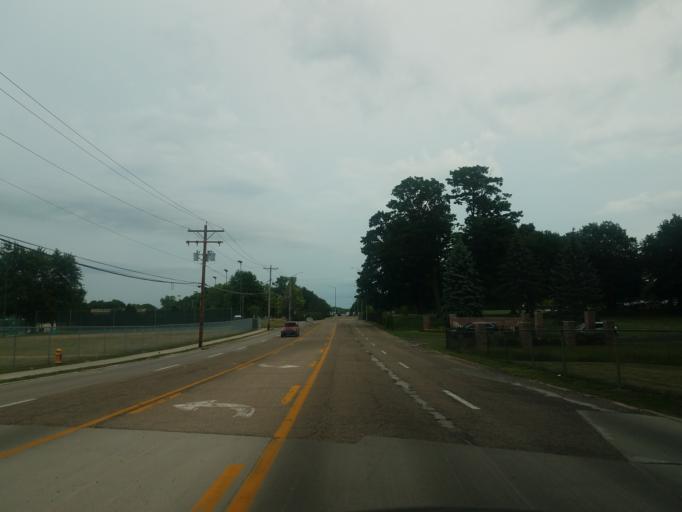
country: US
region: Illinois
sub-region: McLean County
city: Bloomington
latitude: 40.4834
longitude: -88.9731
